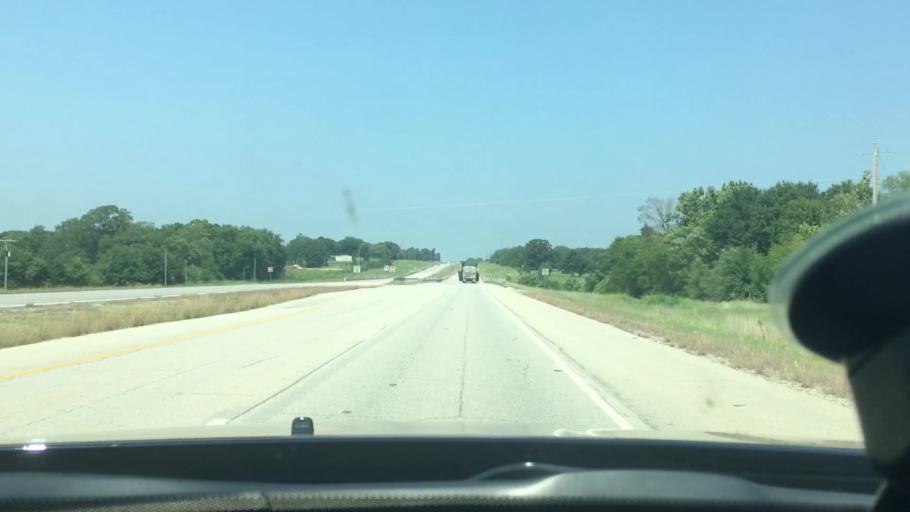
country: US
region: Oklahoma
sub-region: Atoka County
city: Atoka
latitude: 34.3225
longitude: -96.0391
